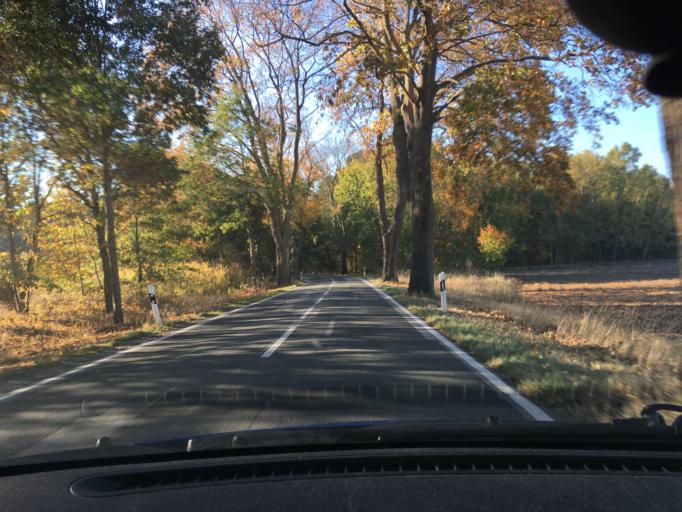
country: DE
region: Lower Saxony
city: Damnatz
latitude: 53.1558
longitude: 11.2103
